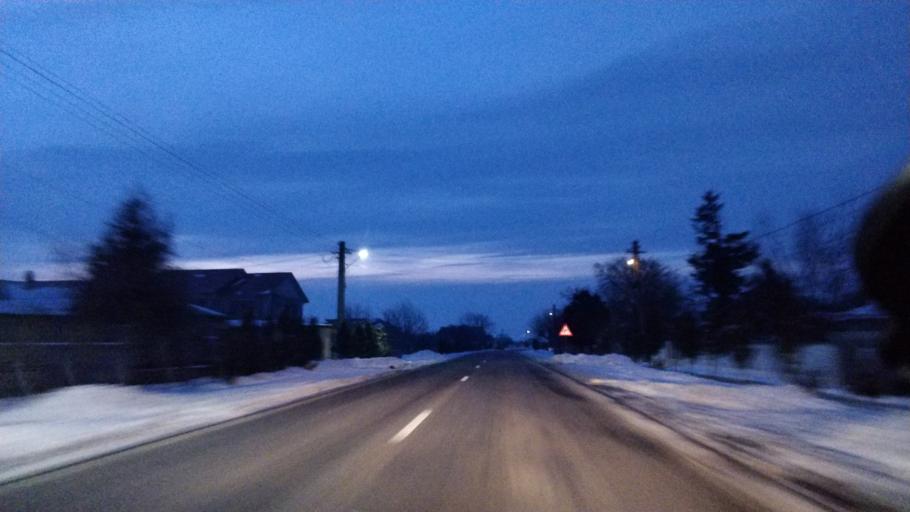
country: RO
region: Vrancea
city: Vulturu de Sus
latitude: 45.6371
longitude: 27.3746
